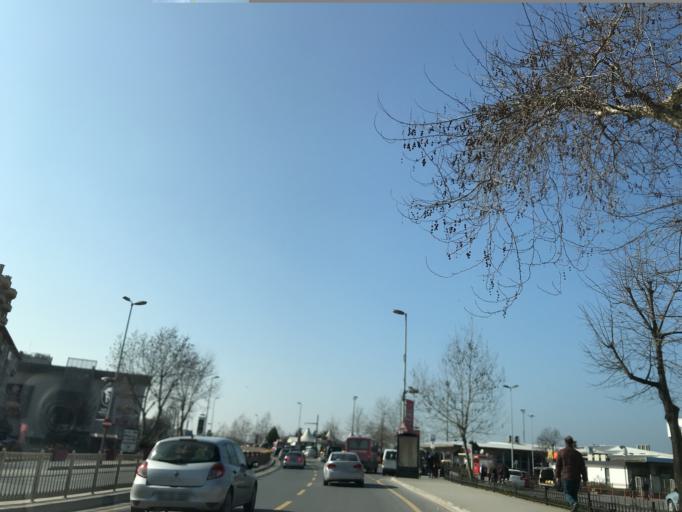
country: TR
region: Yalova
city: Yalova
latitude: 40.6590
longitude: 29.2802
